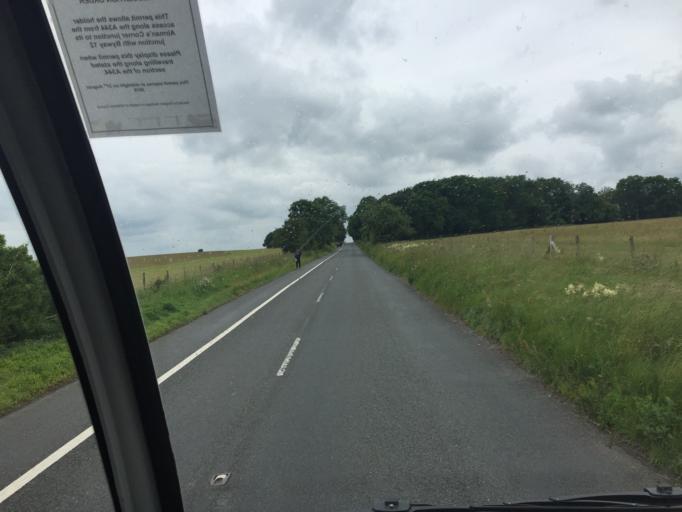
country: GB
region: England
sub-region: Wiltshire
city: Durnford
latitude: 51.1819
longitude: -1.8368
